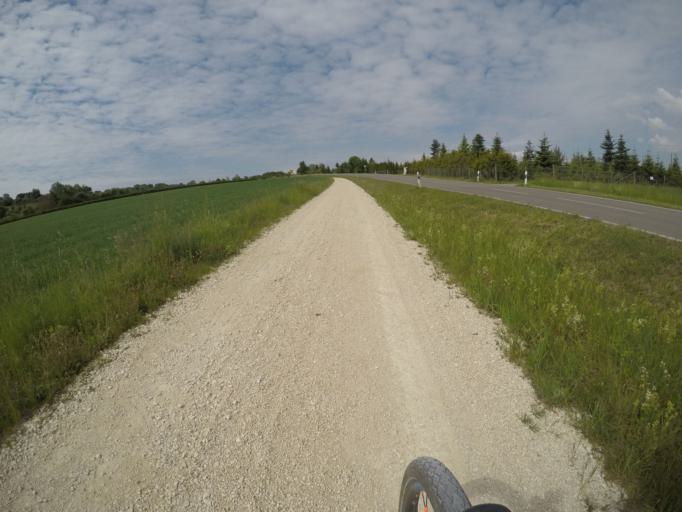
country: DE
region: Baden-Wuerttemberg
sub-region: Regierungsbezirk Stuttgart
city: Notzingen
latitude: 48.6683
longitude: 9.4378
